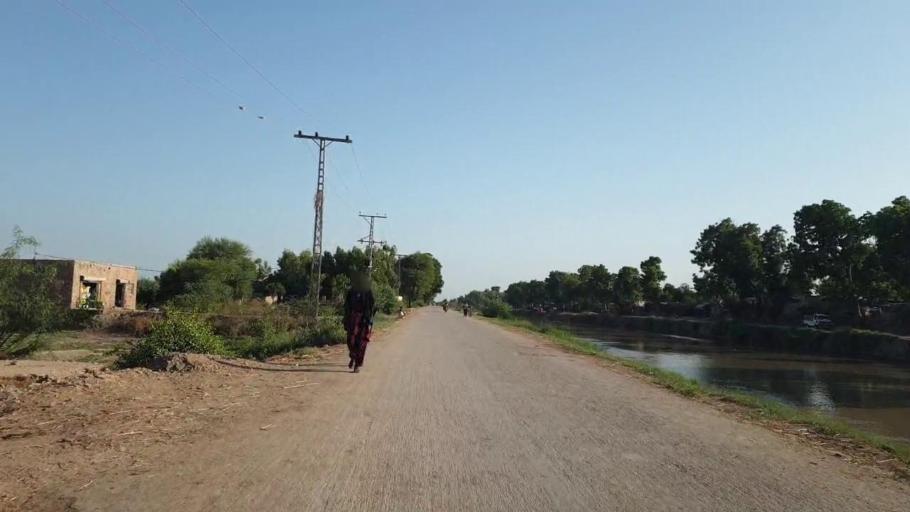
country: PK
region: Sindh
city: Hyderabad
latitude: 25.3145
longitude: 68.4306
